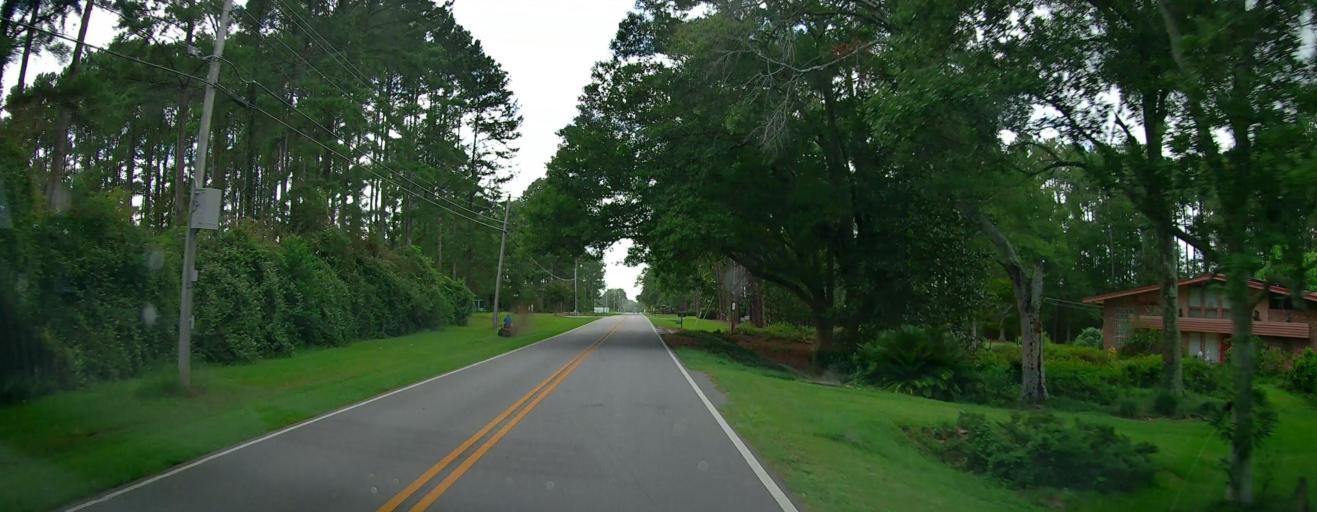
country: US
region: Georgia
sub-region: Ben Hill County
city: Fitzgerald
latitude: 31.7056
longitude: -83.2846
